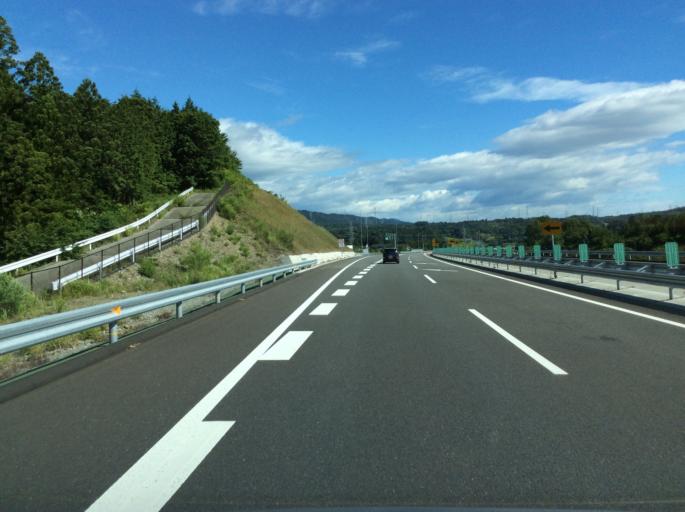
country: JP
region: Fukushima
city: Namie
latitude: 37.4970
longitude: 140.9436
